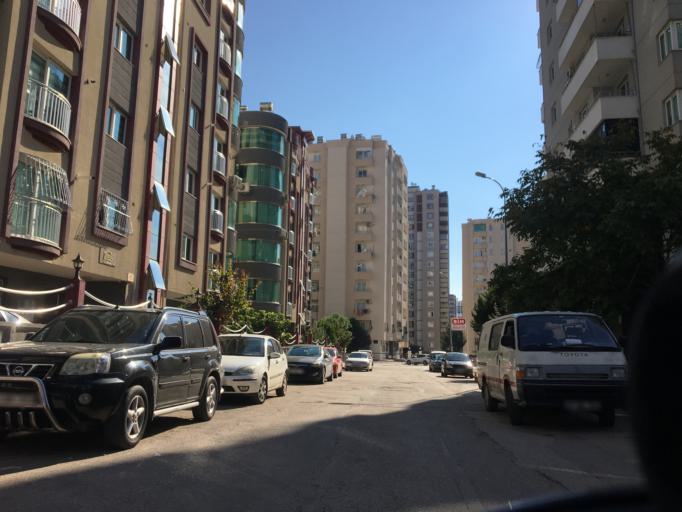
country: TR
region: Adana
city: Seyhan
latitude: 37.0274
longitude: 35.2851
